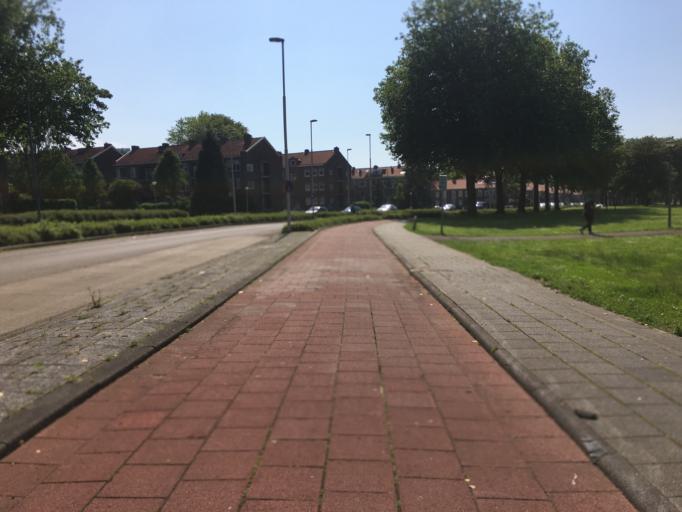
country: NL
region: South Holland
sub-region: Gemeente Rotterdam
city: Rotterdam
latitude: 51.9261
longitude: 4.4952
